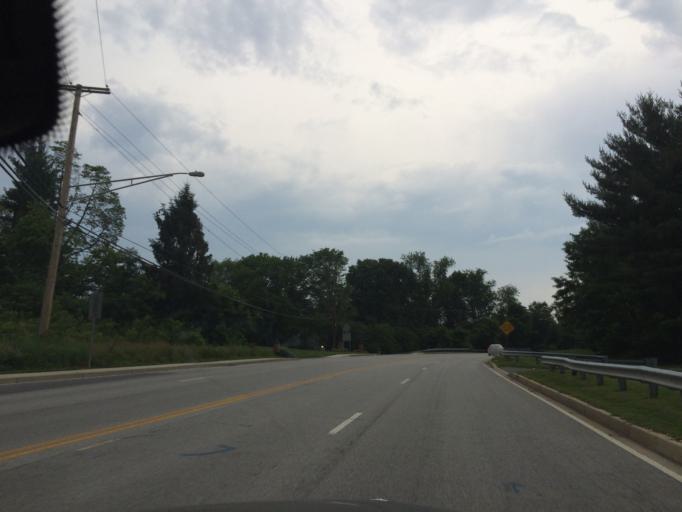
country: US
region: Maryland
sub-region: Howard County
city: Riverside
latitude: 39.1900
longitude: -76.8930
